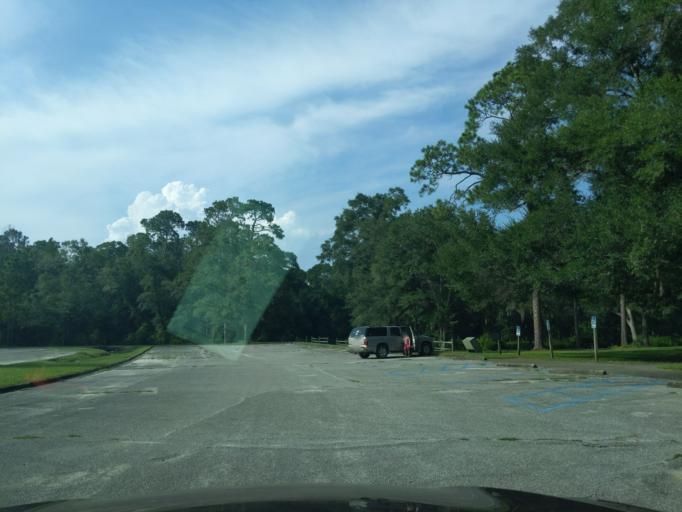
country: US
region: Florida
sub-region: Gadsden County
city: Midway
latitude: 30.4046
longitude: -84.4074
